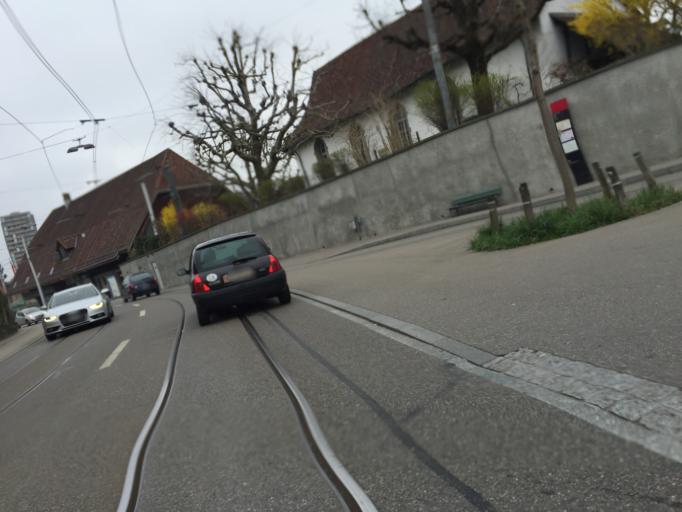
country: CH
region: Bern
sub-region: Bern-Mittelland District
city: Koniz
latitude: 46.9406
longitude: 7.3919
